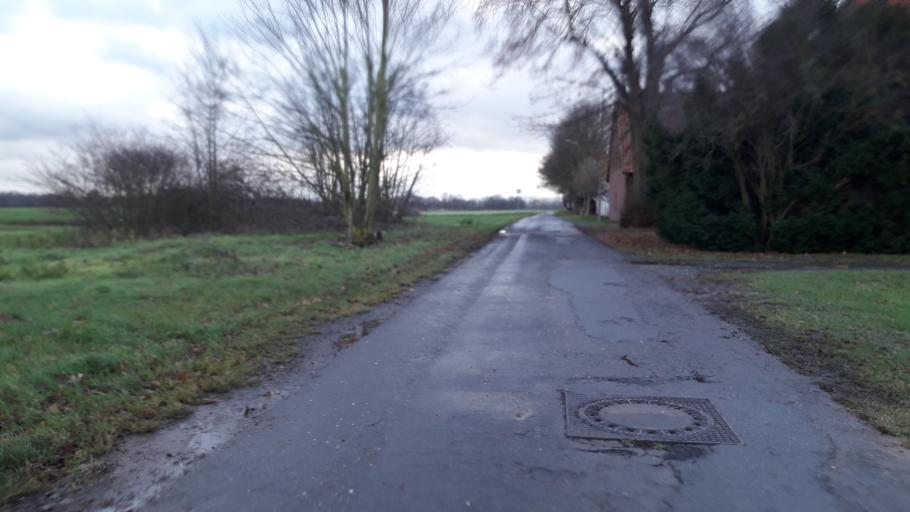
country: DE
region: North Rhine-Westphalia
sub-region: Regierungsbezirk Detmold
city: Petershagen
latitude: 52.3260
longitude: 8.9695
